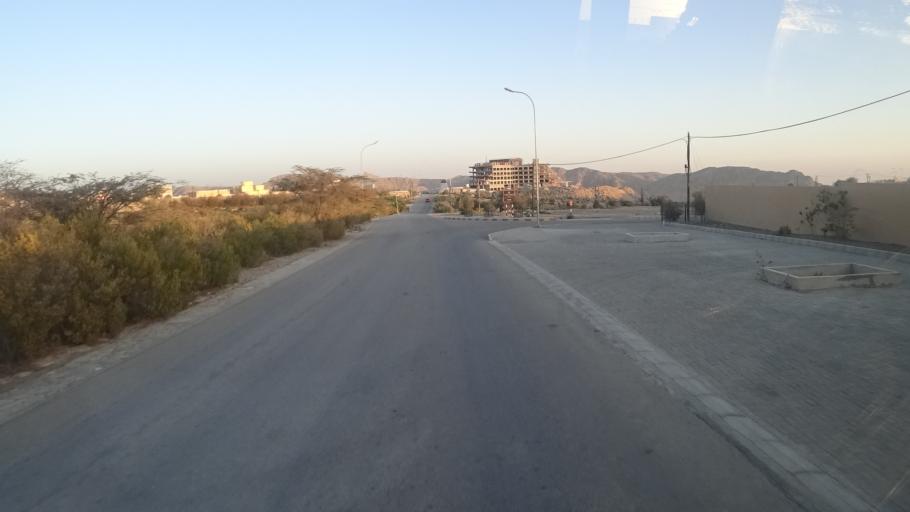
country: OM
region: Muhafazat ad Dakhiliyah
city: Izki
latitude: 23.0695
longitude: 57.6713
